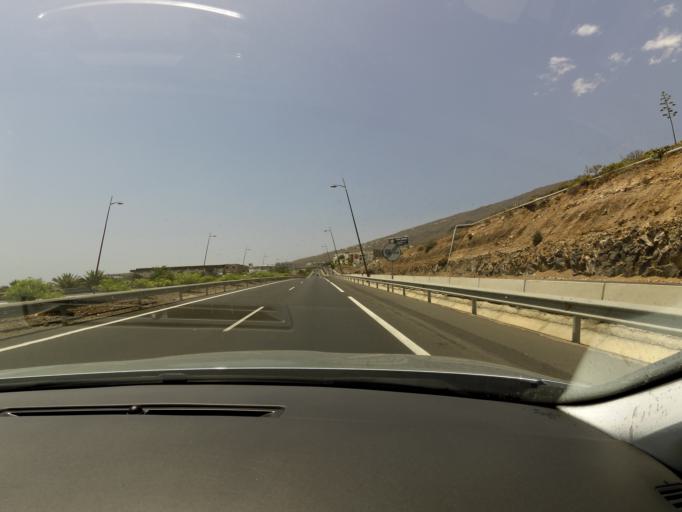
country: ES
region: Canary Islands
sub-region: Provincia de Santa Cruz de Tenerife
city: Adeje
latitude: 28.1161
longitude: -16.7365
